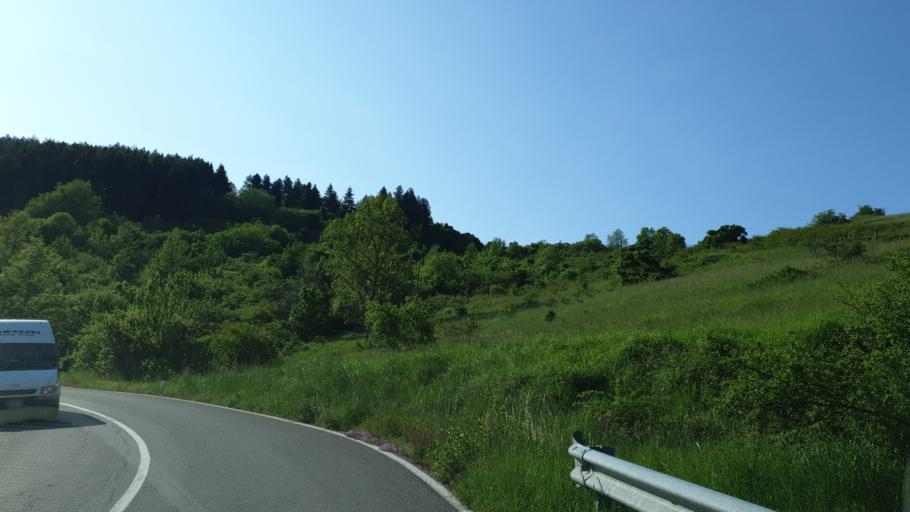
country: IT
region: Tuscany
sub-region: Province of Arezzo
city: Stia
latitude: 43.7823
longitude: 11.6567
